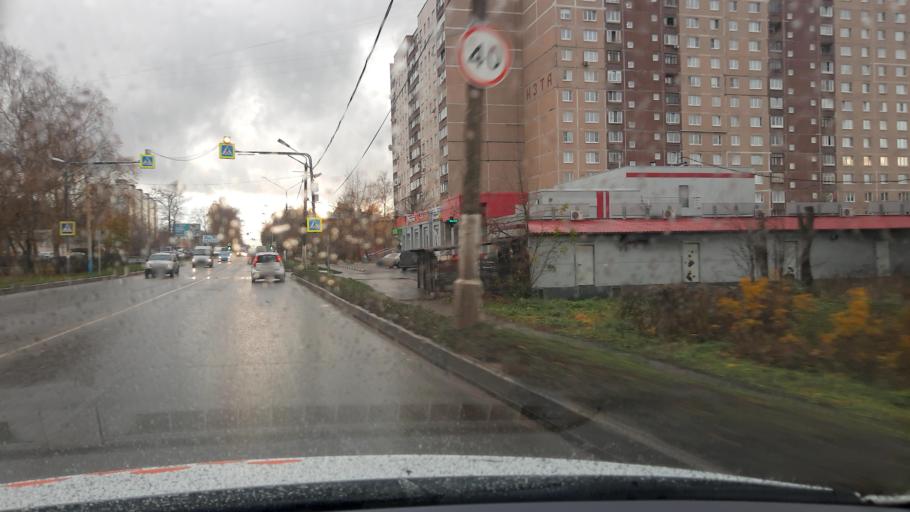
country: RU
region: Moskovskaya
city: Noginsk
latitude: 55.8448
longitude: 38.4102
